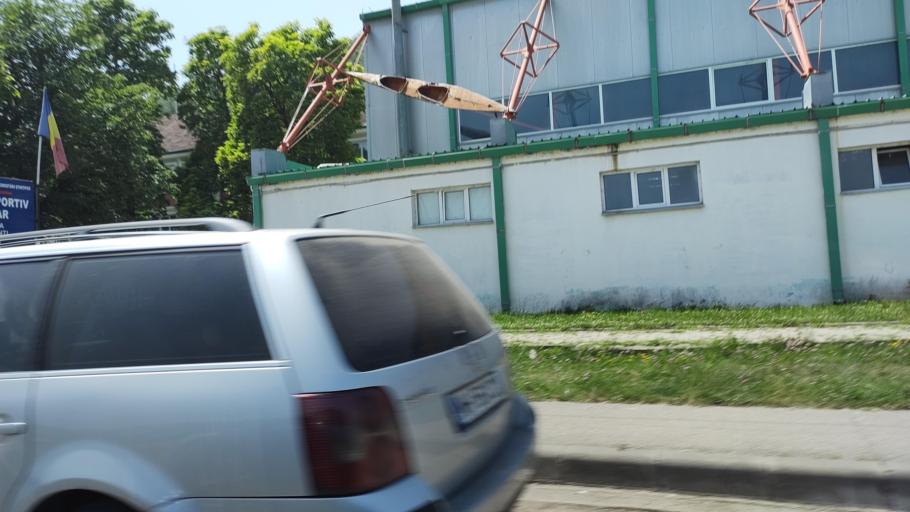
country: RO
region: Mehedinti
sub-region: Municipiul Orsova
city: Orsova
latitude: 44.7330
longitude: 22.4041
